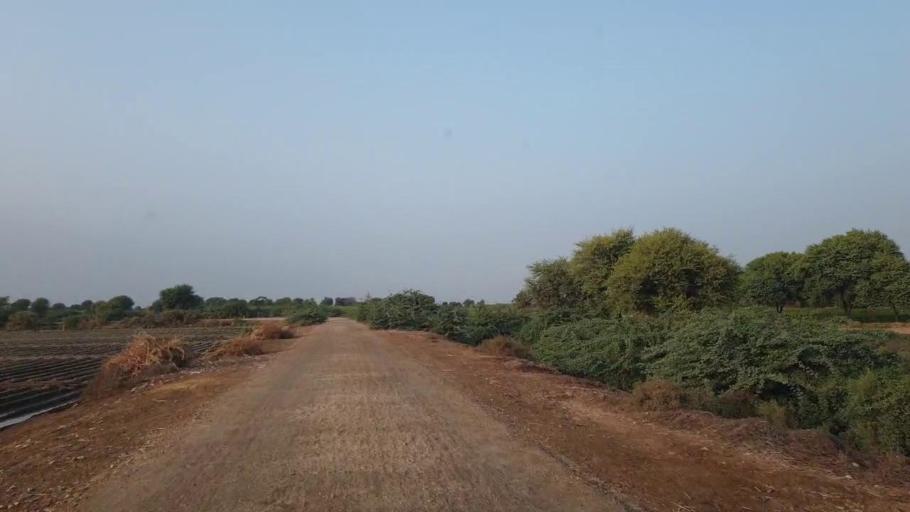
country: PK
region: Sindh
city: Tando Ghulam Ali
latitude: 25.0657
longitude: 68.9605
